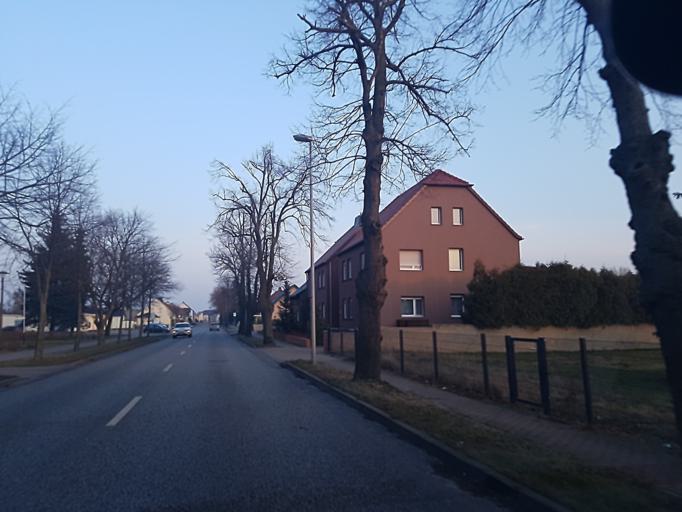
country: DE
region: Saxony-Anhalt
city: Elster
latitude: 51.8298
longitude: 12.8140
